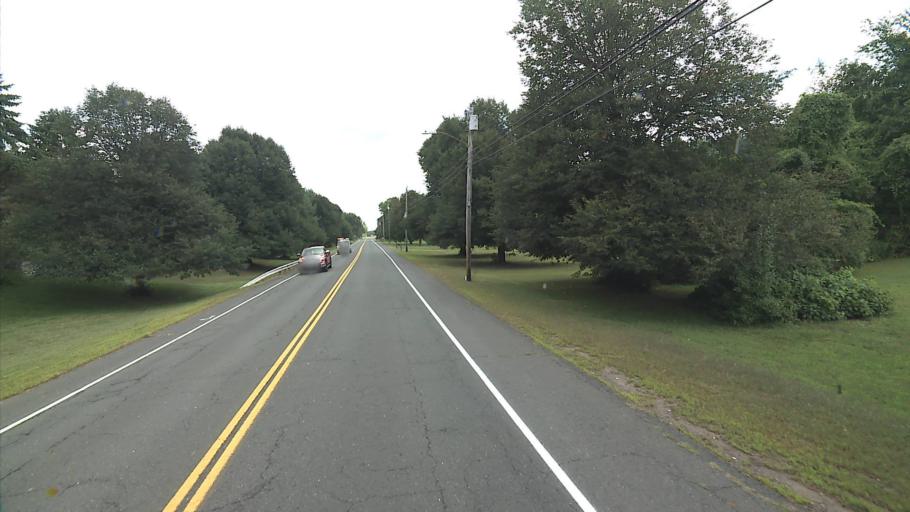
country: US
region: Connecticut
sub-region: Hartford County
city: Tariffville
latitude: 41.8745
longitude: -72.7443
